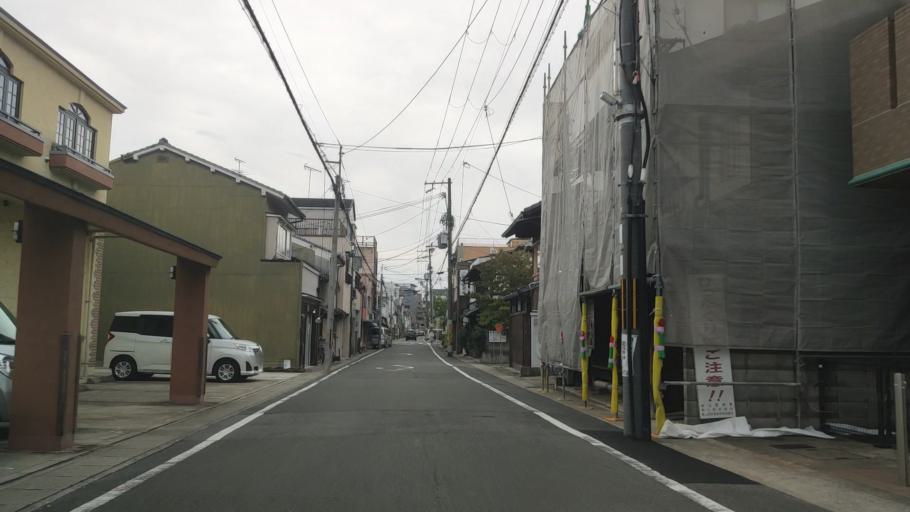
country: JP
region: Kyoto
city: Kyoto
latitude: 34.9922
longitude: 135.7697
